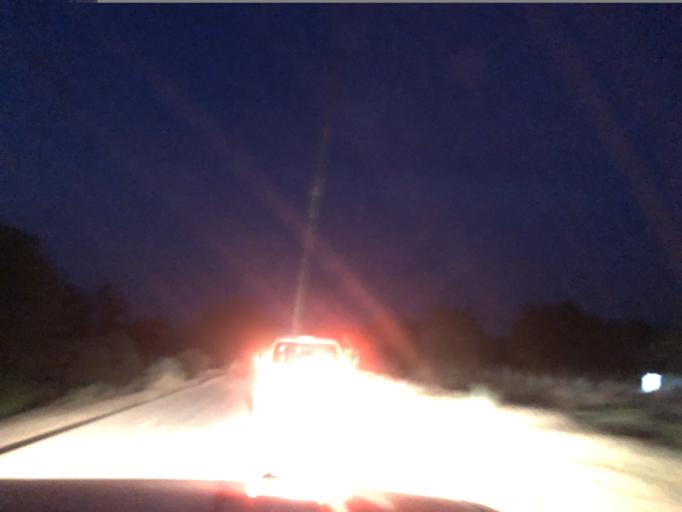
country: TD
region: Mayo-Kebbi Est
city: Guelendeng
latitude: 11.4194
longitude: 15.3227
